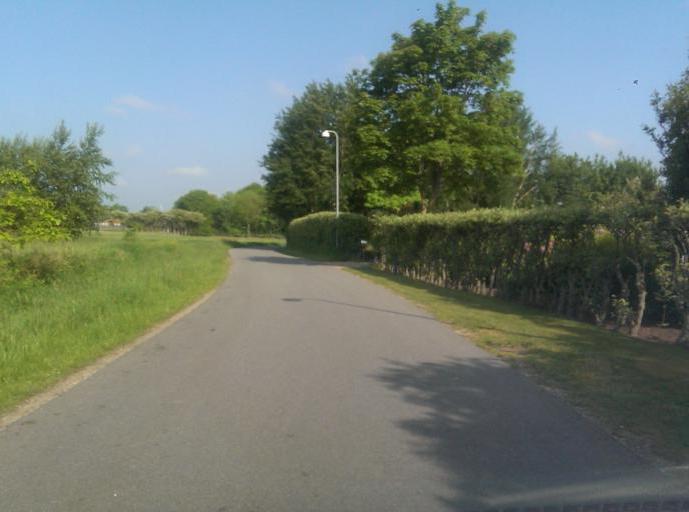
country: DK
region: South Denmark
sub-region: Esbjerg Kommune
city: Tjaereborg
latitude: 55.4585
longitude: 8.5920
